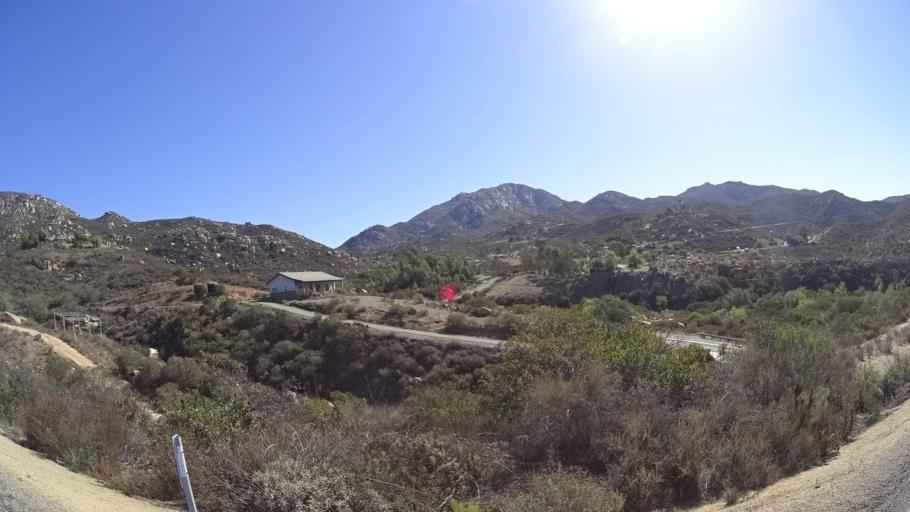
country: US
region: California
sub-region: San Diego County
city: Jamul
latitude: 32.7089
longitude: -116.7985
